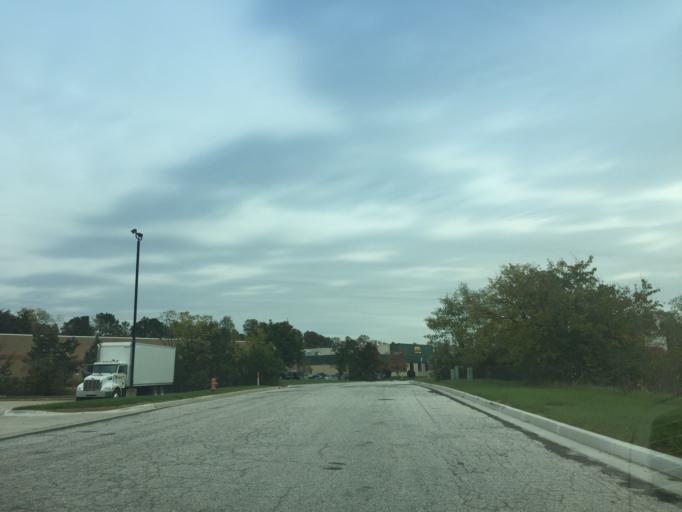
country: US
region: Maryland
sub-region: Baltimore County
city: Rossville
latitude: 39.3378
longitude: -76.4754
